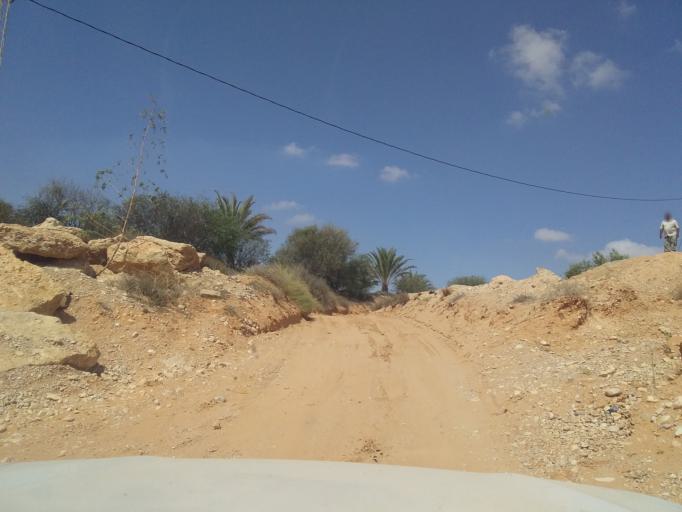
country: TN
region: Madanin
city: Medenine
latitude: 33.6021
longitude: 10.3186
